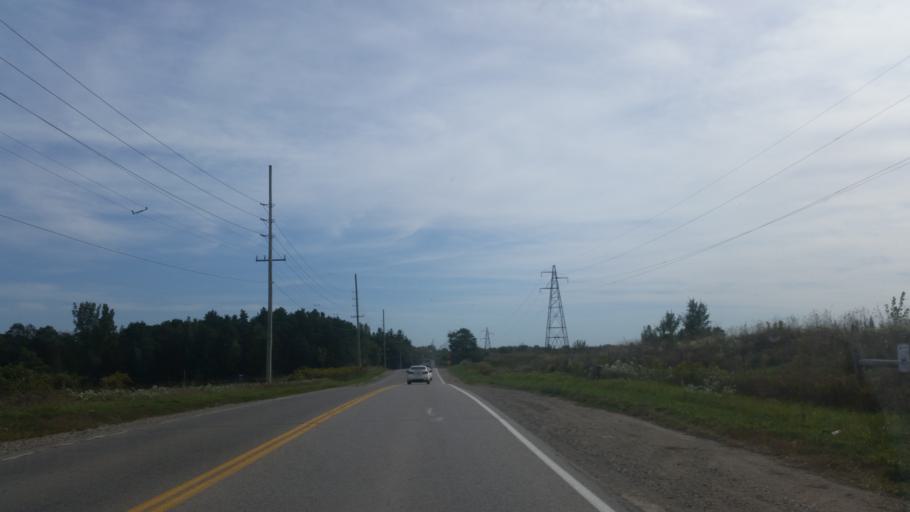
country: CA
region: Ontario
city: London
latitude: 43.0612
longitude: -81.2037
